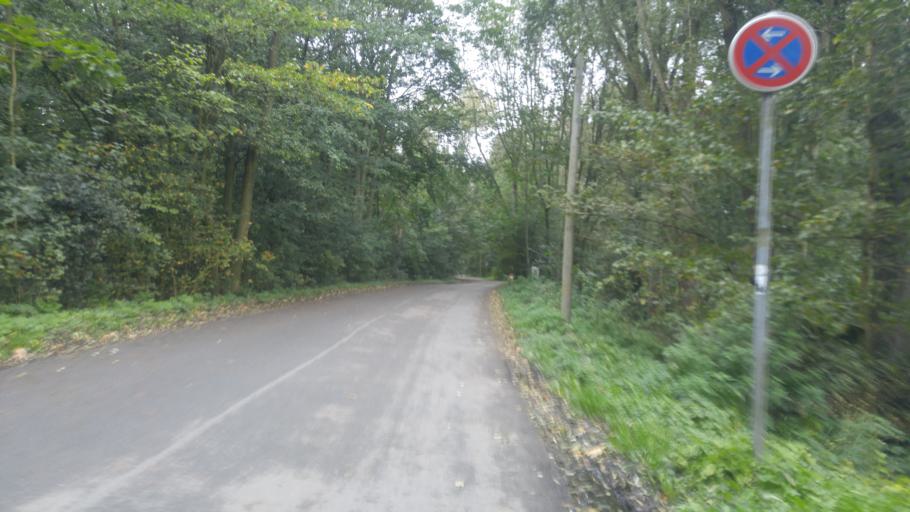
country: DE
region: Bremen
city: Bremen
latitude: 53.1068
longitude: 8.8393
